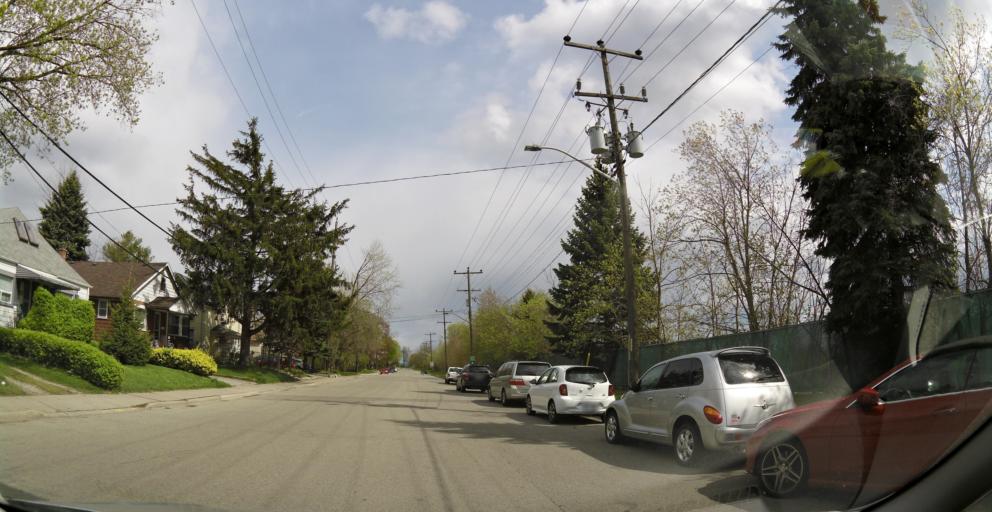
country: CA
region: Ontario
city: Mississauga
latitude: 43.5472
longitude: -79.5882
